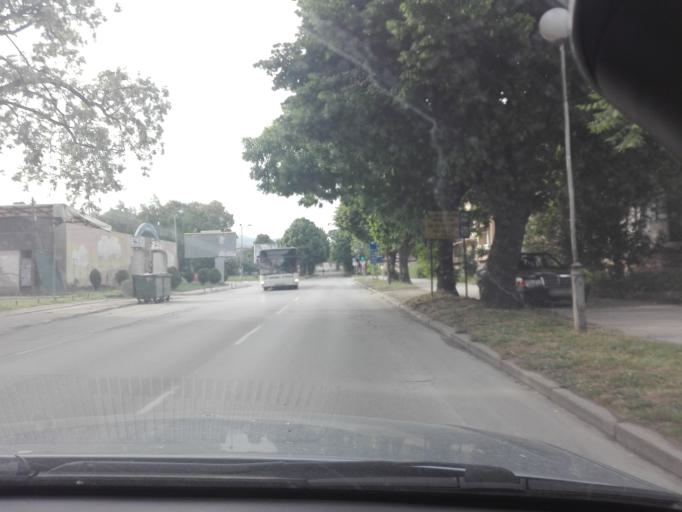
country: MK
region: Bitola
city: Bitola
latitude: 41.0229
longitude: 21.3396
